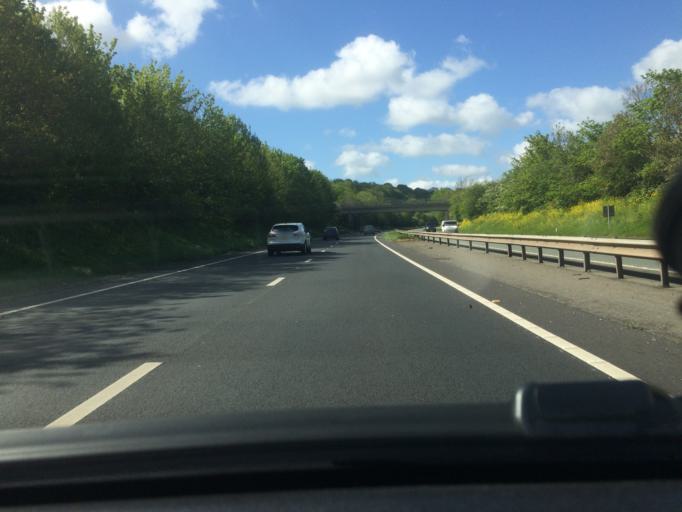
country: GB
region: Wales
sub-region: Wrexham
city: Gresford
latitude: 53.0956
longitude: -2.9673
